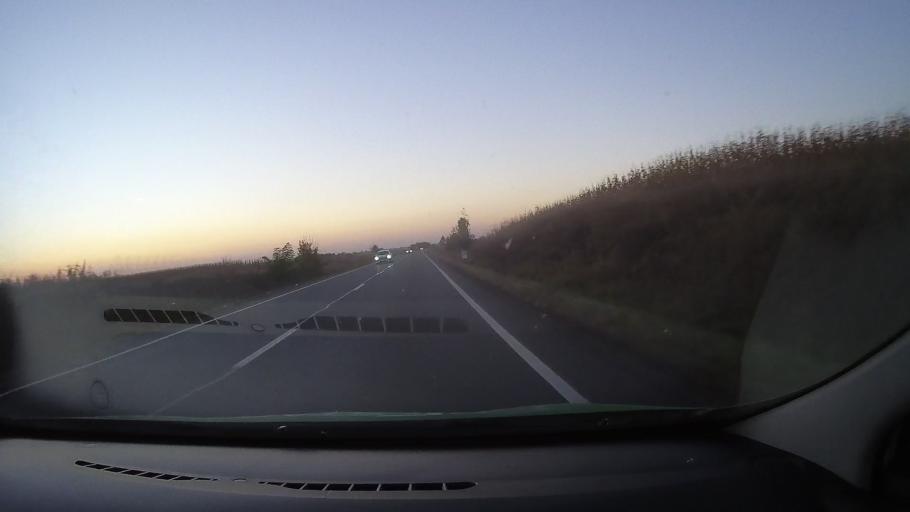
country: RO
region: Bihor
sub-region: Comuna Tarcea
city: Tarcea
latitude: 47.4369
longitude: 22.1989
